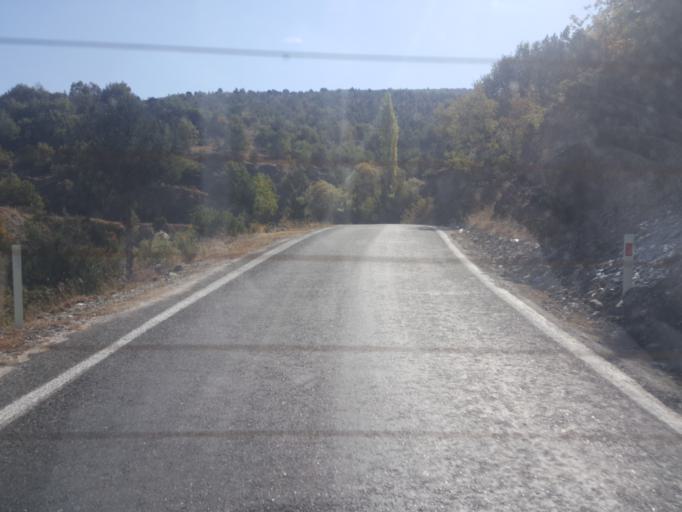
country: TR
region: Kastamonu
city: Tosya
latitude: 40.9945
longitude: 34.1662
